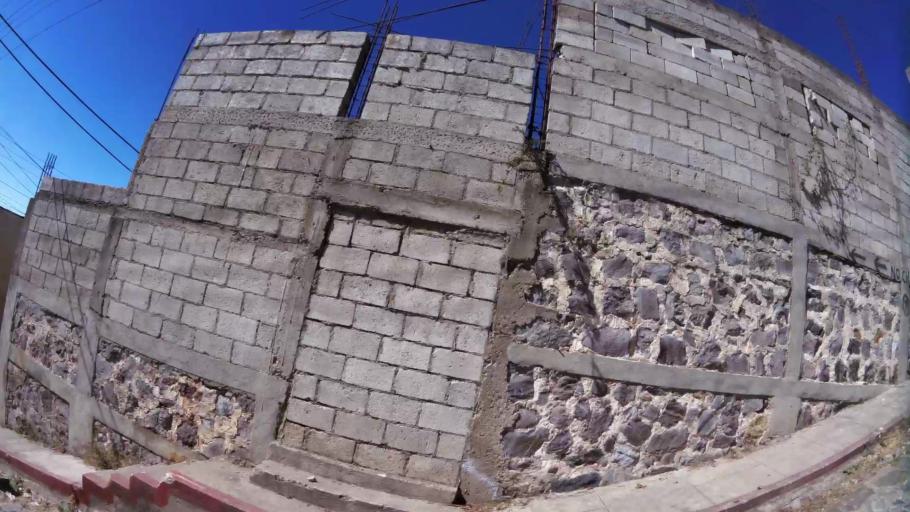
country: GT
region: Solola
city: Solola
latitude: 14.7682
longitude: -91.1822
